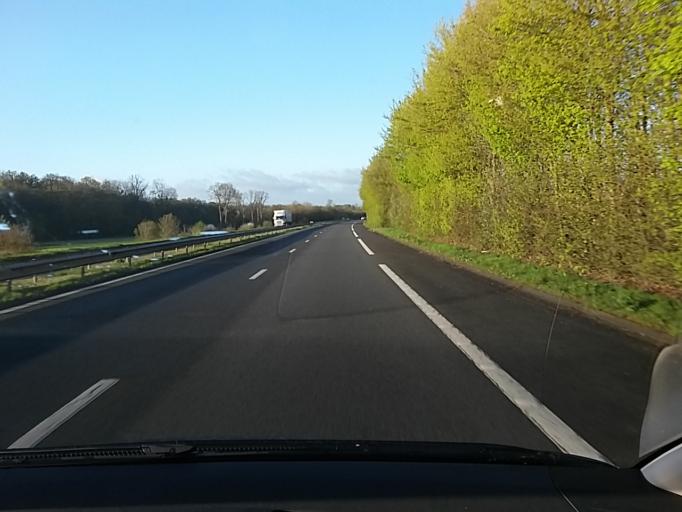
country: FR
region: Picardie
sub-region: Departement de l'Oise
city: Jaux
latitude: 49.3739
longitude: 2.7804
